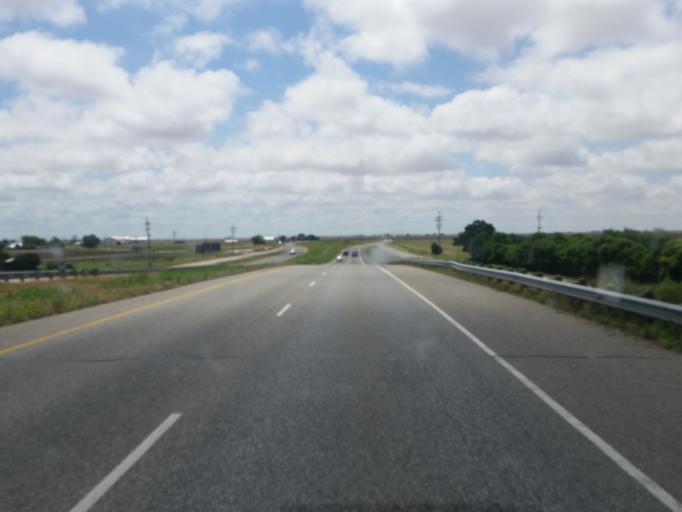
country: US
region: Texas
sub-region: Lubbock County
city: Slaton
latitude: 33.4198
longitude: -101.6426
